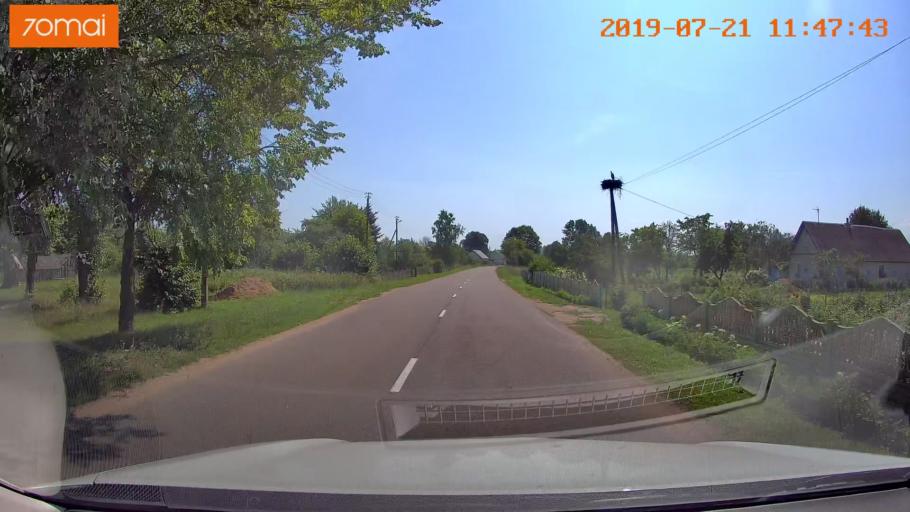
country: BY
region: Grodnenskaya
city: Lyubcha
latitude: 53.9015
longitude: 26.0518
